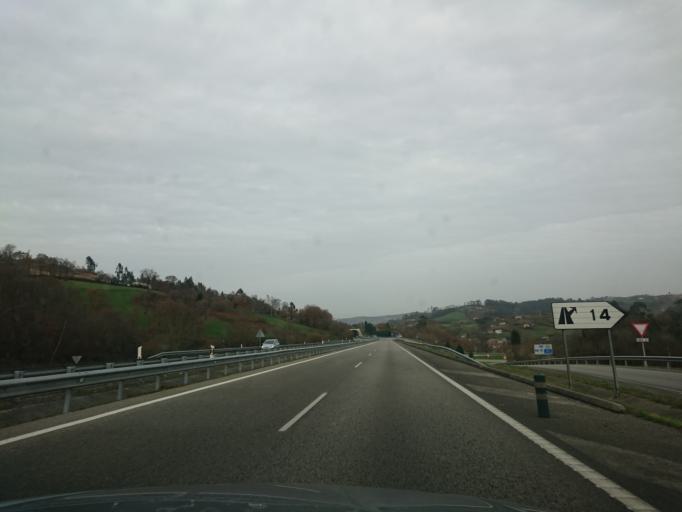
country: ES
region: Asturias
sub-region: Province of Asturias
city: Pola de Siero
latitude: 43.3534
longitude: -5.6809
